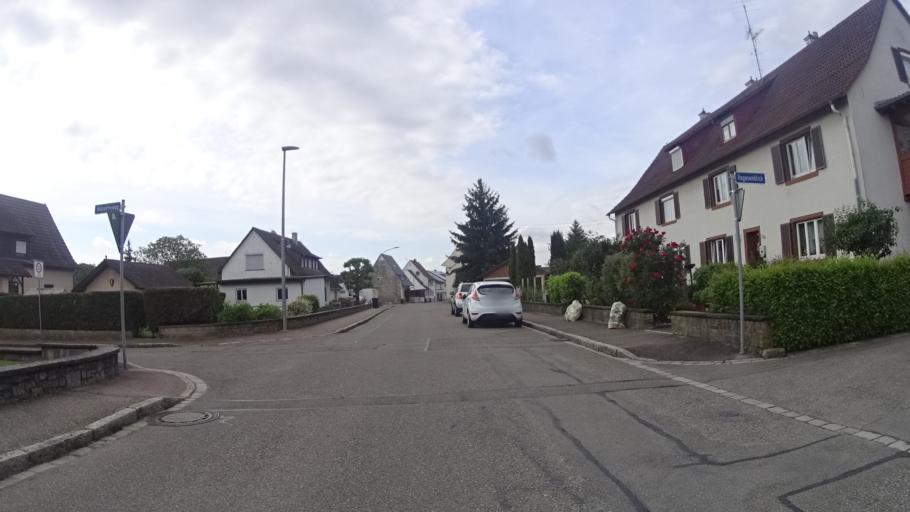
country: DE
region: Baden-Wuerttemberg
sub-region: Freiburg Region
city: Schliengen
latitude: 47.7698
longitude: 7.5531
